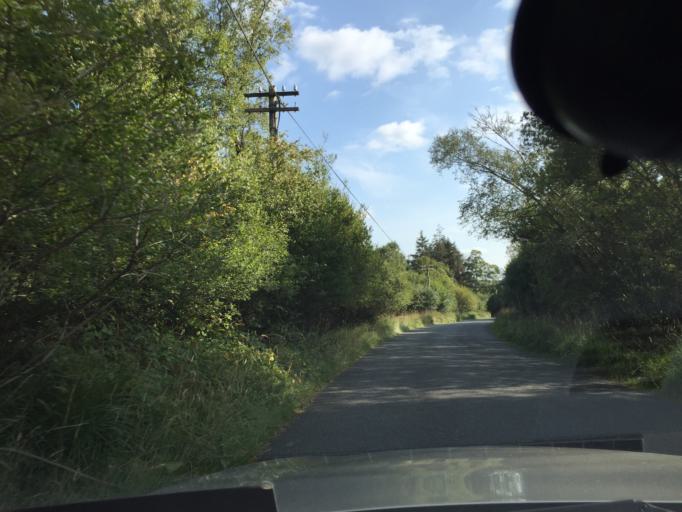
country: IE
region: Leinster
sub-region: Wicklow
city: Rathdrum
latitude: 53.0185
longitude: -6.3030
